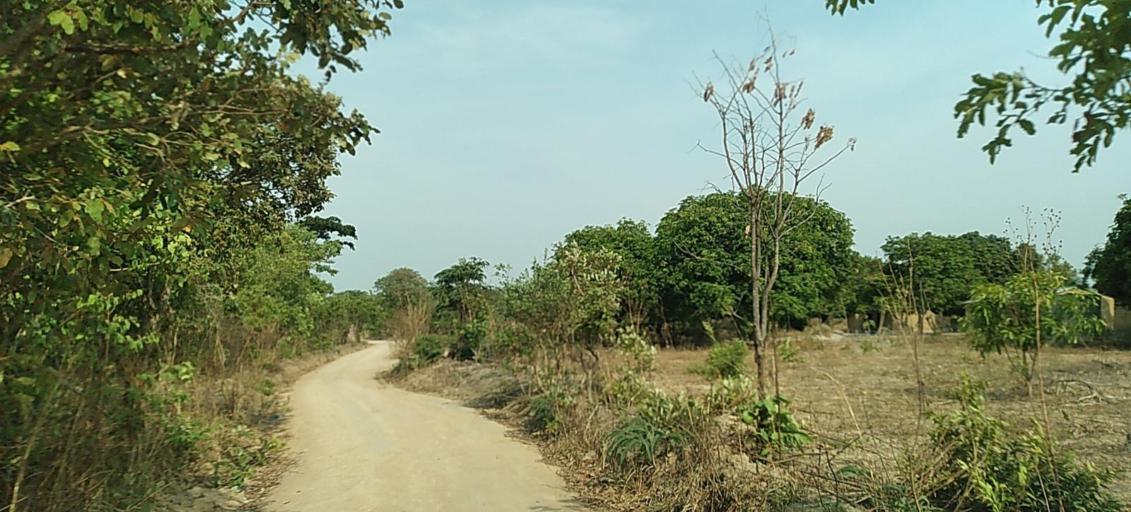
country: ZM
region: Copperbelt
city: Ndola
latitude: -13.2231
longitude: 28.6739
